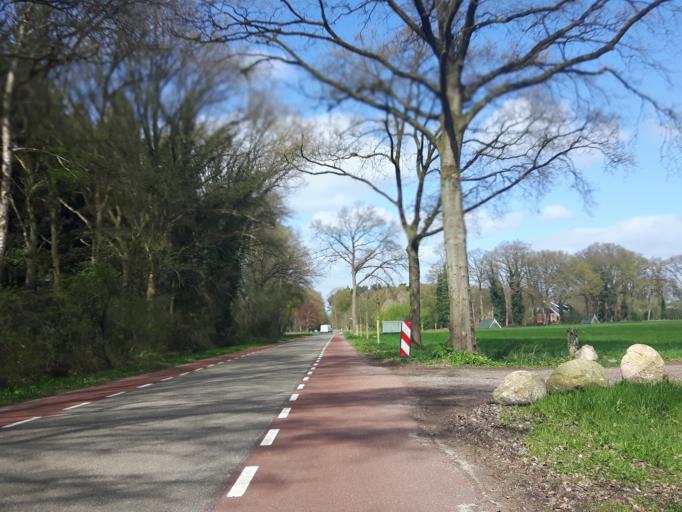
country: NL
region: Overijssel
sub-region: Gemeente Hengelo
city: Hengelo
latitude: 52.2220
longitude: 6.8313
